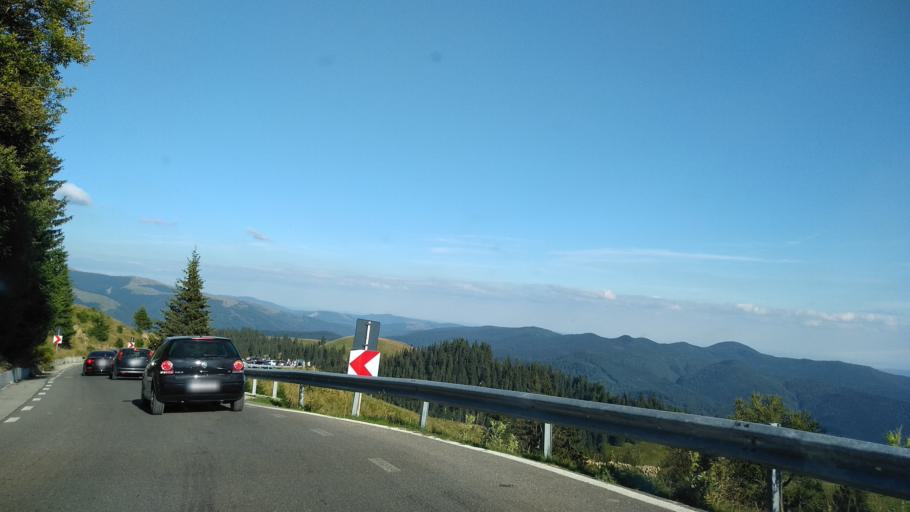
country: RO
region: Prahova
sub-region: Oras Sinaia
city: Sinaia
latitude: 45.3198
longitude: 25.4818
